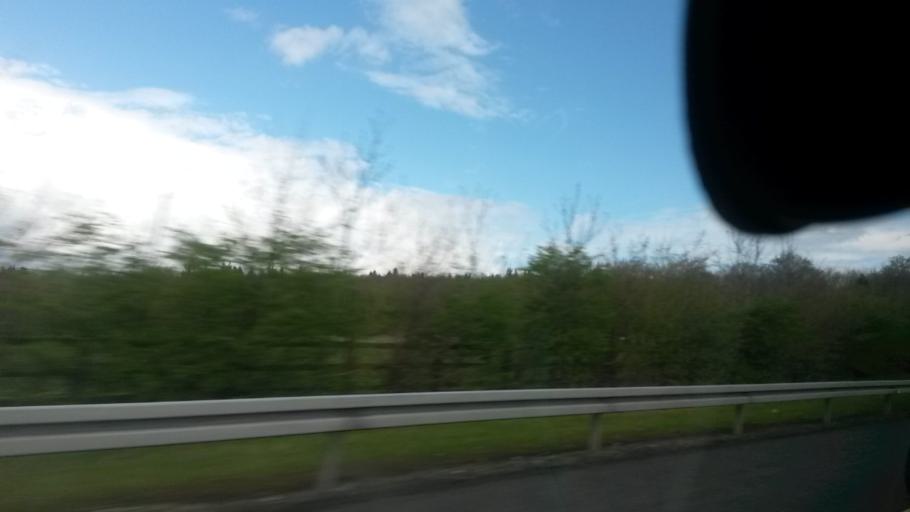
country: IE
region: Leinster
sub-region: Kildare
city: Monasterevin
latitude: 53.1171
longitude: -7.0474
